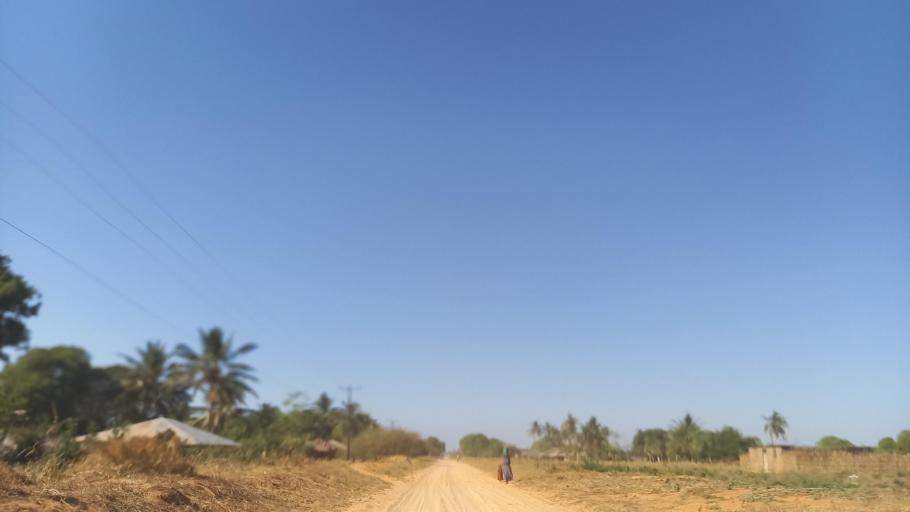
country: MZ
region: Cabo Delgado
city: Pemba
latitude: -13.1497
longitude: 40.5571
